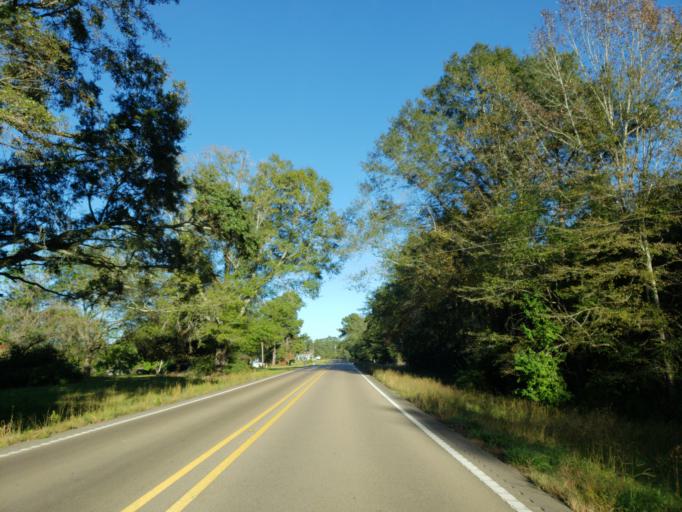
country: US
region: Mississippi
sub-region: Perry County
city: Richton
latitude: 31.3754
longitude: -88.8604
